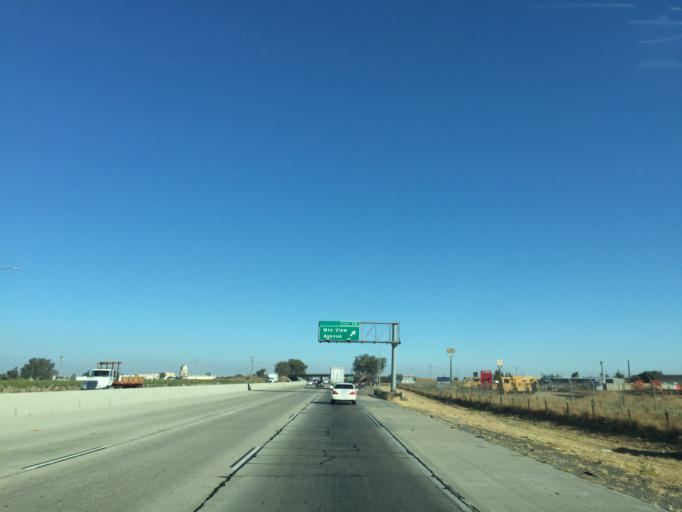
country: US
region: California
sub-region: Fresno County
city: Selma
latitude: 36.5507
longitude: -119.6007
